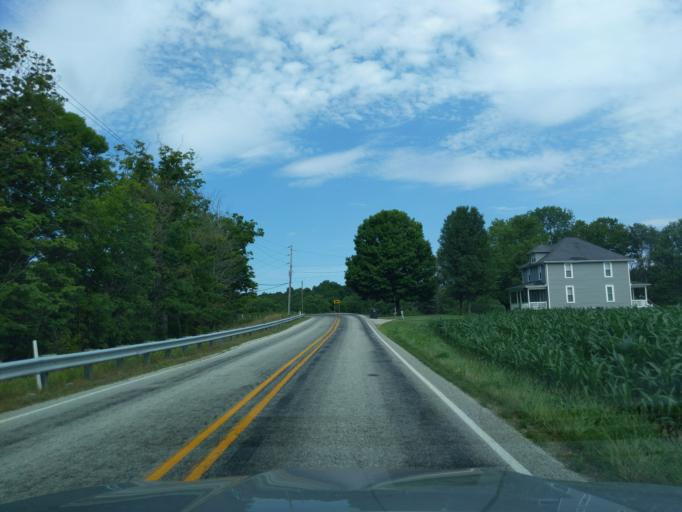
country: US
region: Indiana
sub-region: Ripley County
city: Osgood
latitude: 39.1950
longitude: -85.2549
